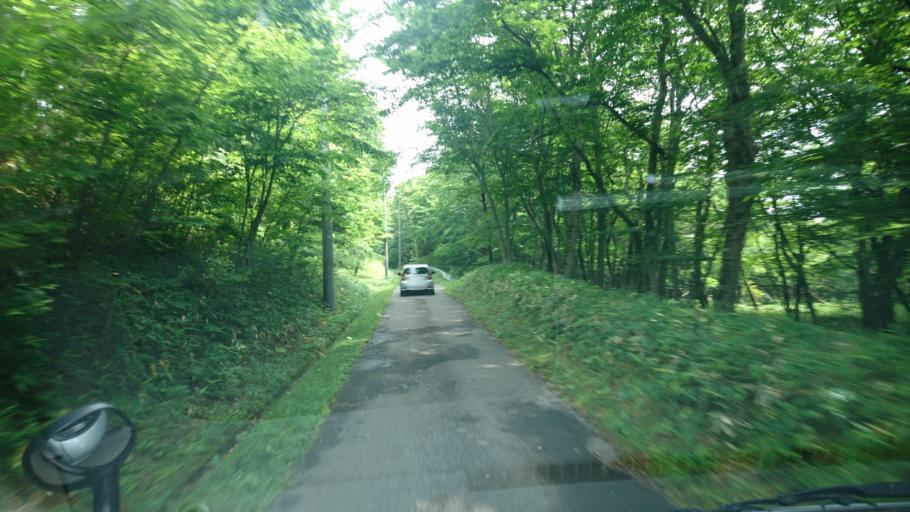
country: JP
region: Iwate
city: Ofunato
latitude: 39.1652
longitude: 141.7496
